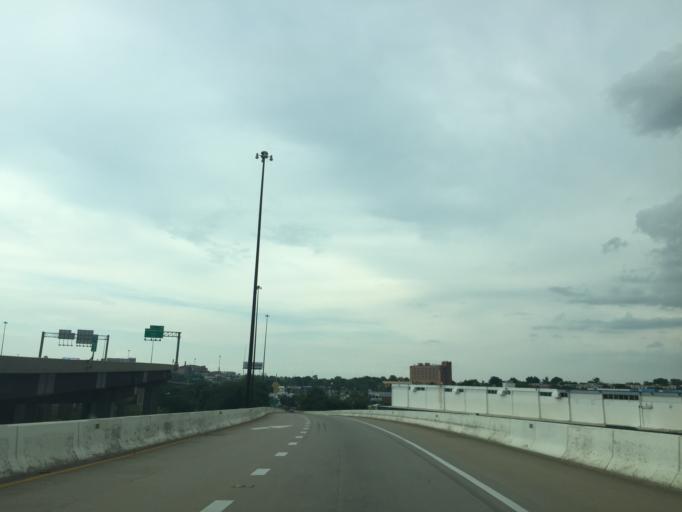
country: US
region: Maryland
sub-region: Baltimore County
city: Dundalk
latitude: 39.2744
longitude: -76.5523
